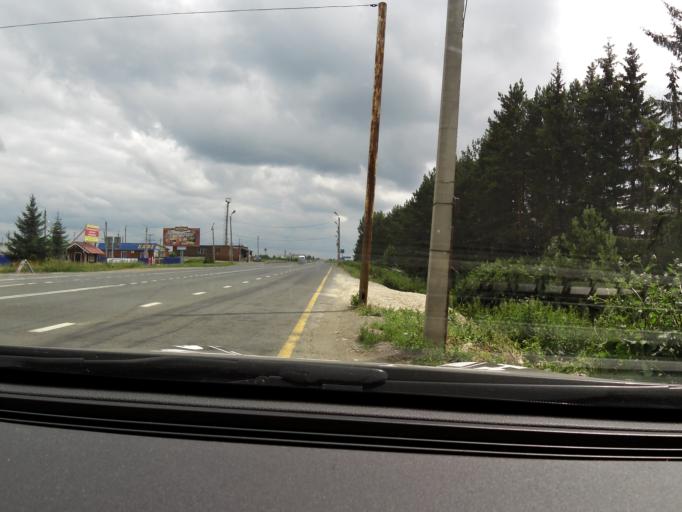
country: RU
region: Perm
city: Kungur
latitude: 57.4085
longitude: 56.8775
